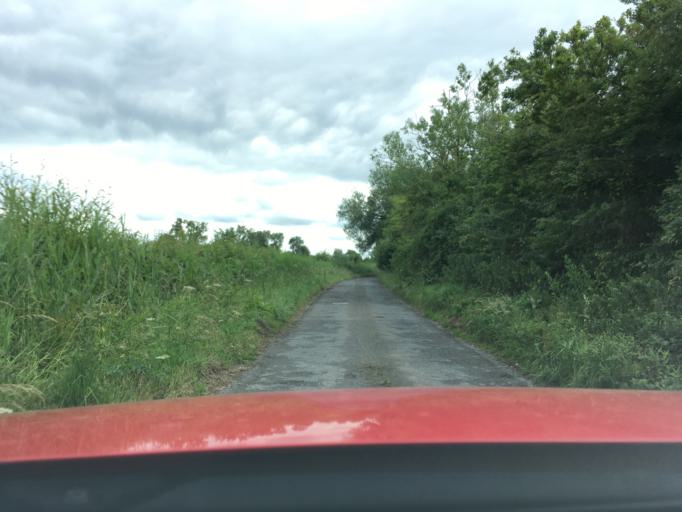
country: GB
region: England
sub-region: Gloucestershire
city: Cinderford
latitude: 51.8041
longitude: -2.4209
